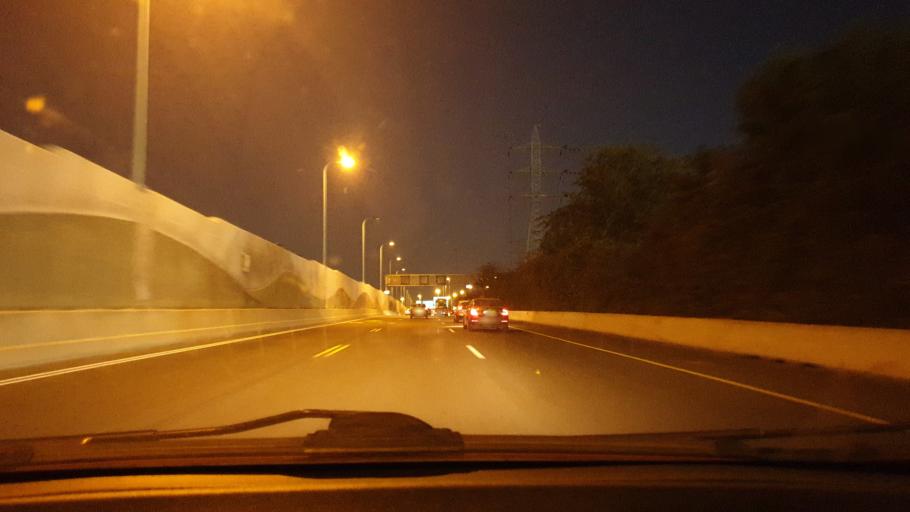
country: IL
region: Tel Aviv
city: Yafo
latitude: 32.0379
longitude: 34.7652
